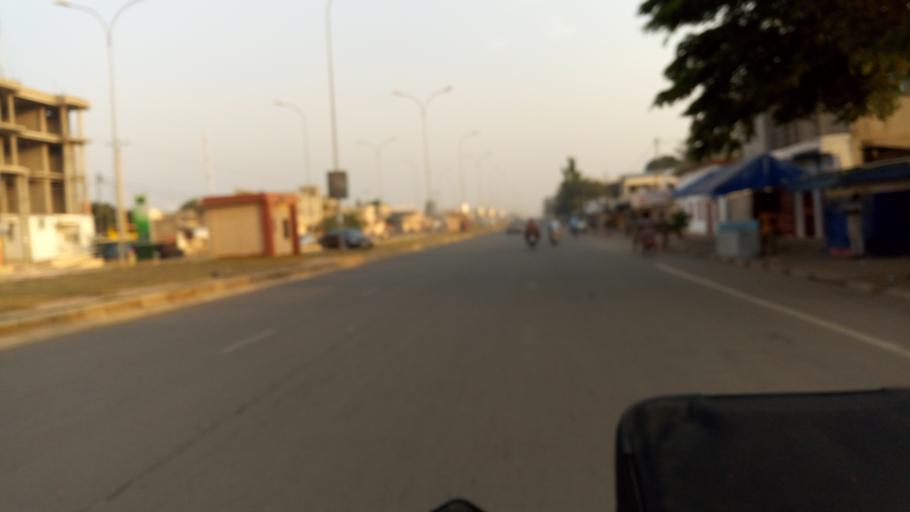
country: TG
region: Maritime
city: Lome
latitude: 6.2014
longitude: 1.1815
